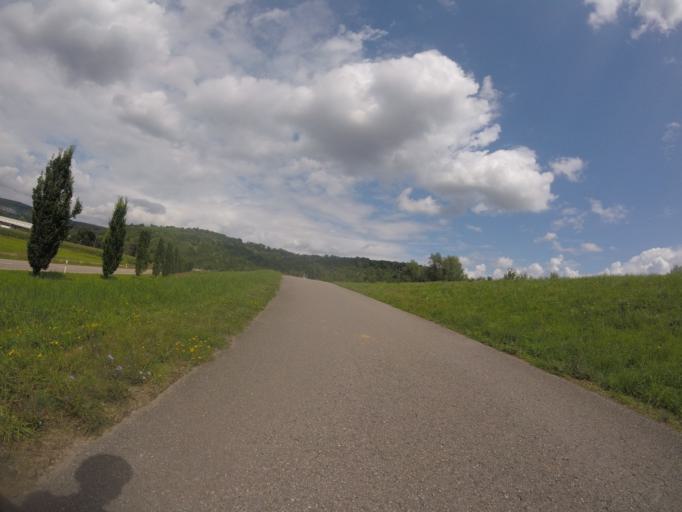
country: DE
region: Baden-Wuerttemberg
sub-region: Regierungsbezirk Stuttgart
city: Winterbach
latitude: 48.8024
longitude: 9.4905
